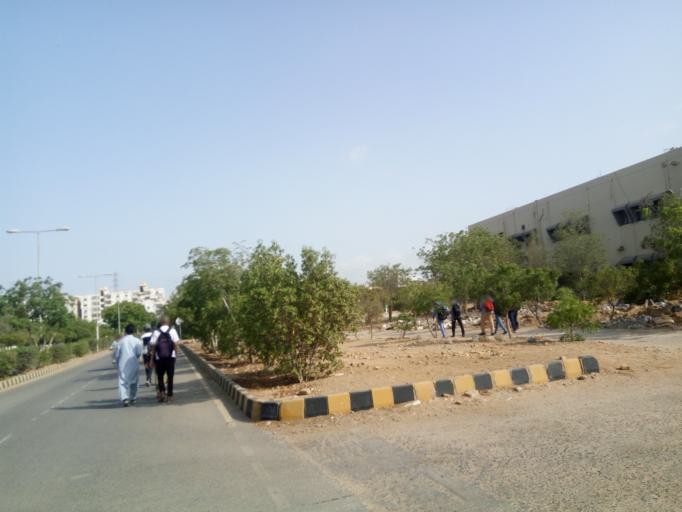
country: PK
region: Sindh
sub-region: Karachi District
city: Karachi
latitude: 24.9318
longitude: 67.1144
